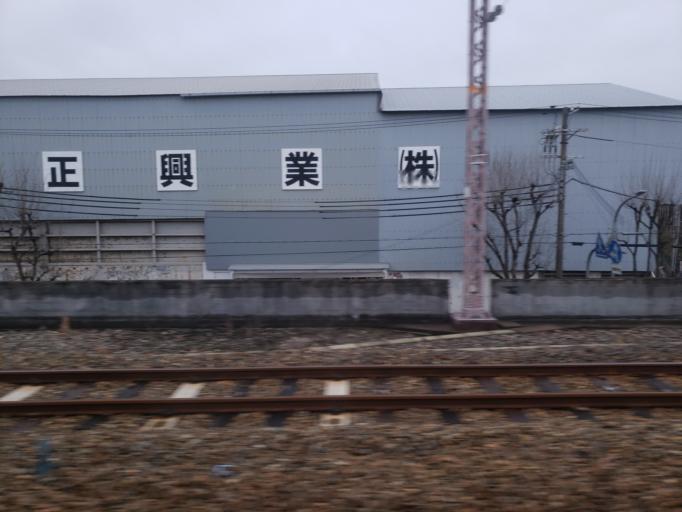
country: JP
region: Hyogo
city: Kobe
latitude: 34.6626
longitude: 135.1547
